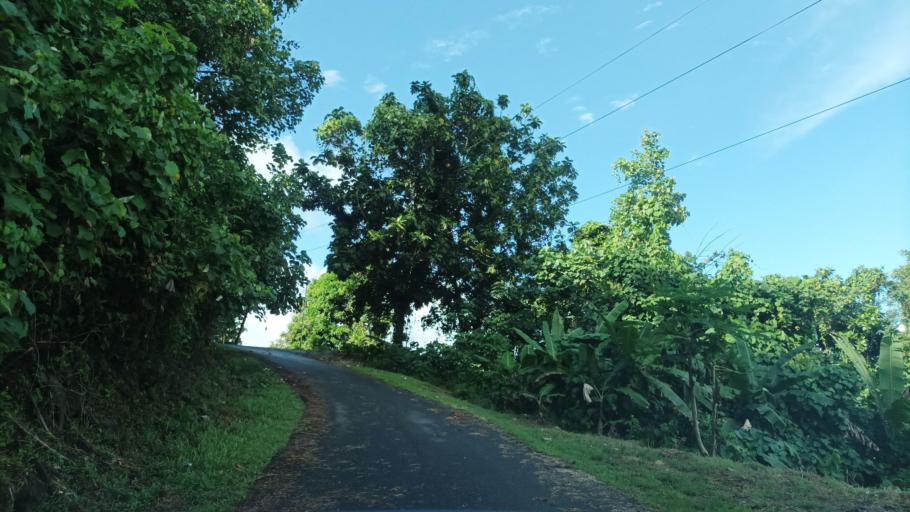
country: FM
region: Pohnpei
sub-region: Kolonia Municipality
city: Kolonia Town
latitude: 6.9644
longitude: 158.1936
